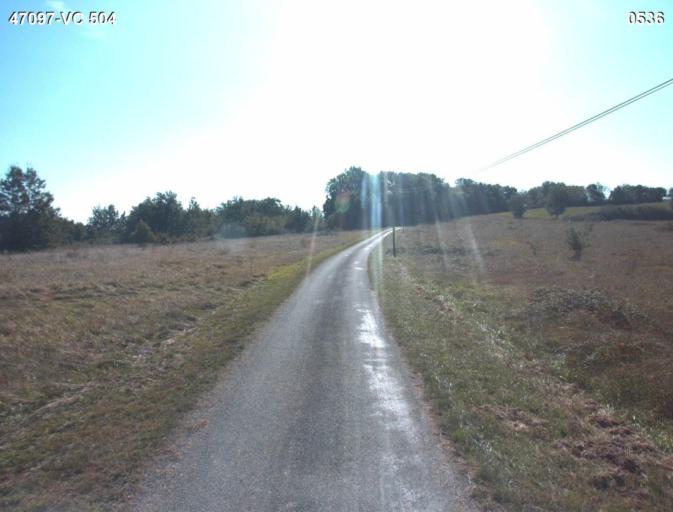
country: FR
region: Aquitaine
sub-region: Departement du Lot-et-Garonne
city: Vianne
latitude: 44.1883
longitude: 0.3512
